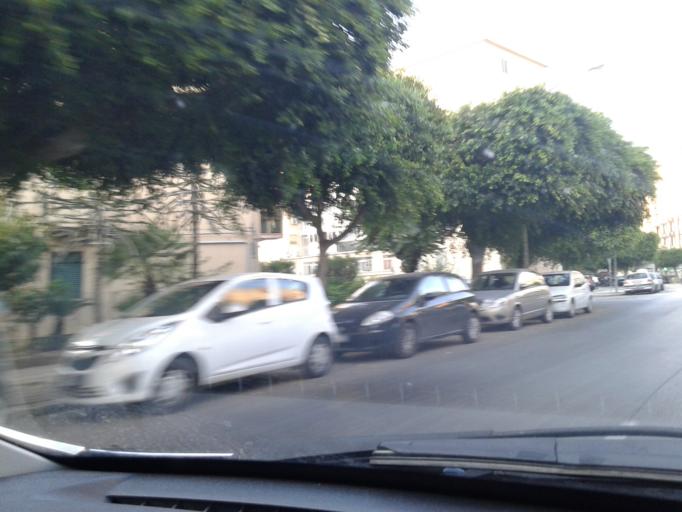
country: IT
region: Sicily
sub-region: Palermo
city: Palermo
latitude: 38.0988
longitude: 13.3356
